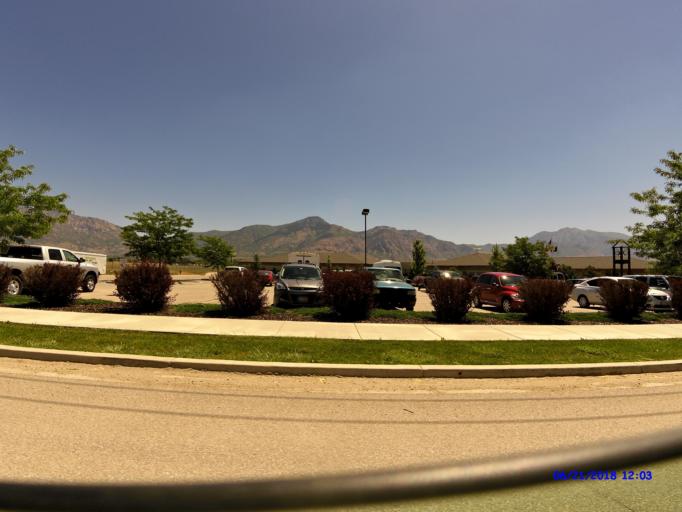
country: US
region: Utah
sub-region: Weber County
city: Harrisville
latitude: 41.2781
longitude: -112.0086
